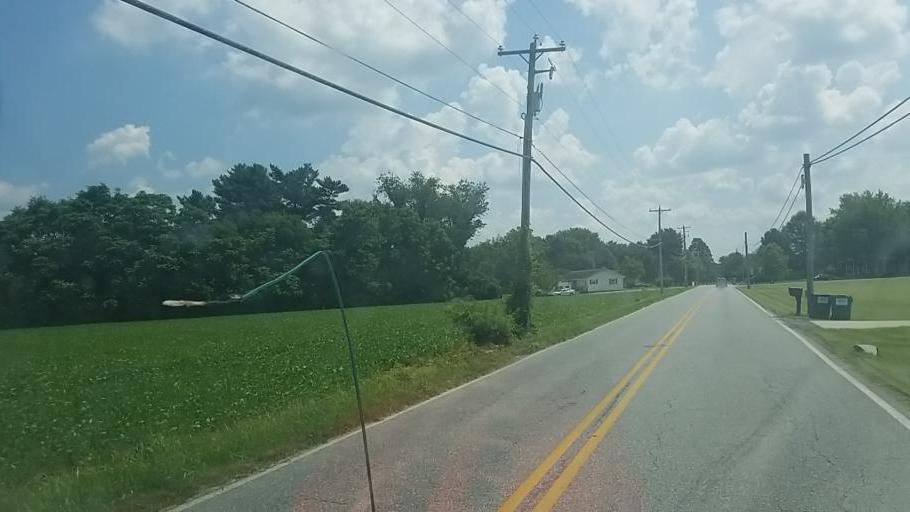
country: US
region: Maryland
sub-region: Wicomico County
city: Salisbury
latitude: 38.3714
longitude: -75.5489
